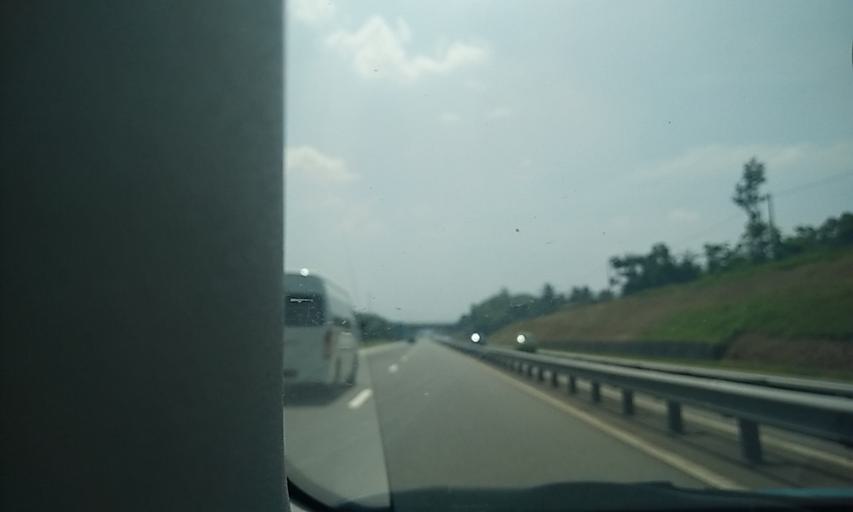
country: LK
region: Western
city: Horana South
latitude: 6.7317
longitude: 79.9991
